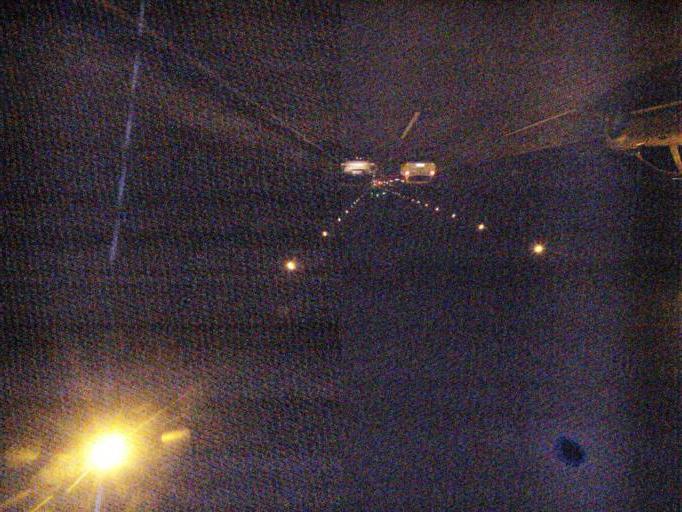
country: BR
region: Rio de Janeiro
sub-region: Rio De Janeiro
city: Rio de Janeiro
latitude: -22.9534
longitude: -43.2051
